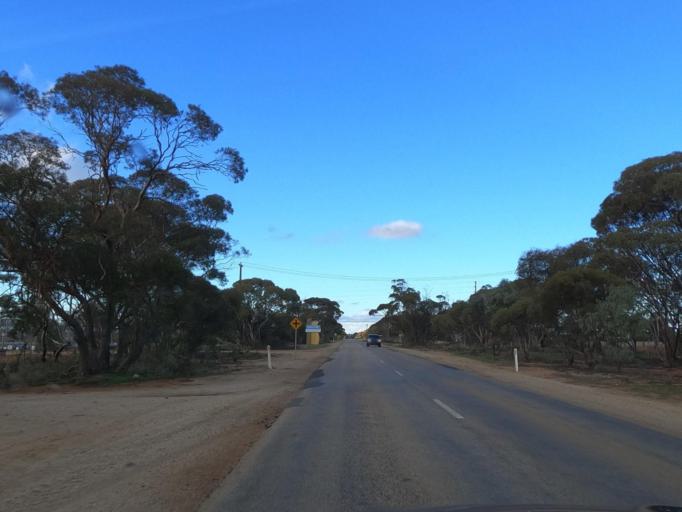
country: AU
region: Victoria
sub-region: Swan Hill
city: Swan Hill
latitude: -35.3464
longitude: 143.5215
